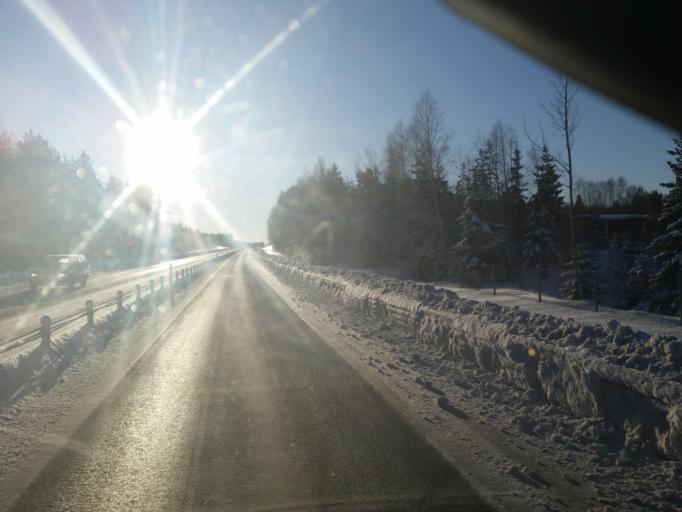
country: SE
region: Norrbotten
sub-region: Pitea Kommun
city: Pitea
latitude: 65.2832
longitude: 21.4422
